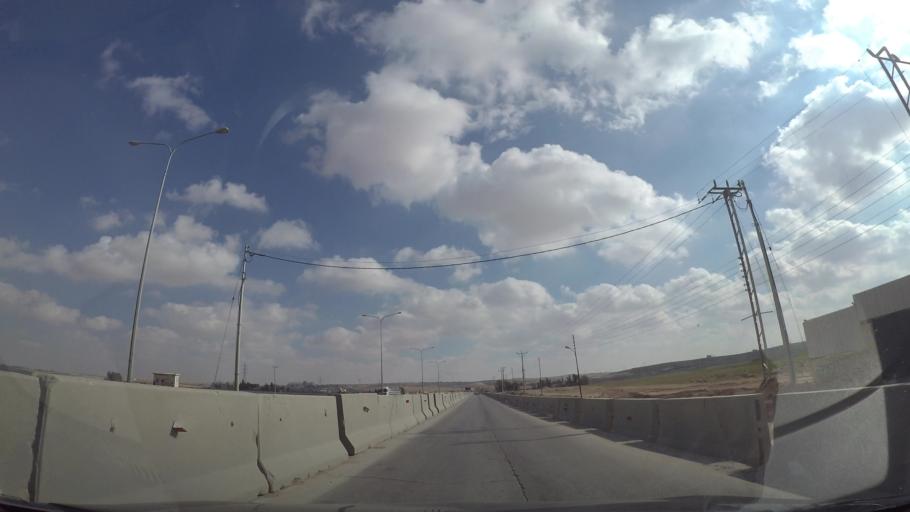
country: JO
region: Amman
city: Al Jizah
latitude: 31.6386
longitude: 35.9831
